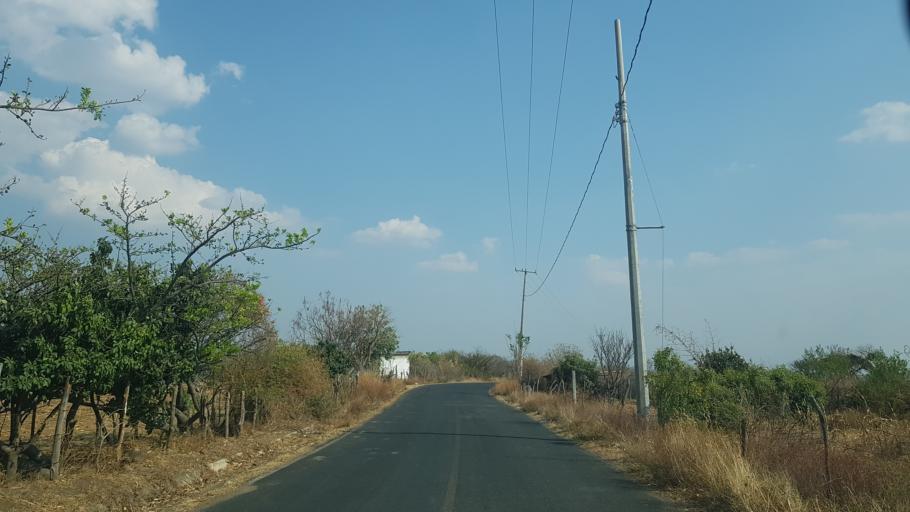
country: MX
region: Morelos
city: Tlacotepec
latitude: 18.8043
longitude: -98.7138
